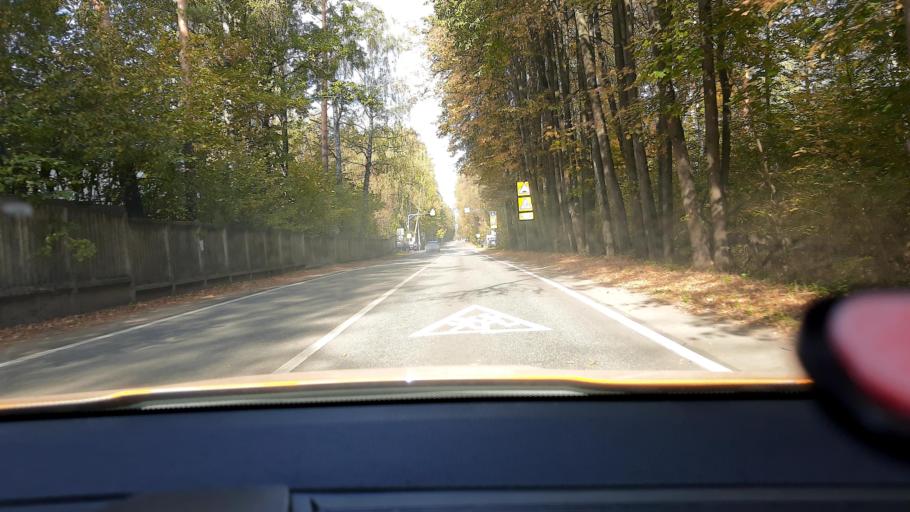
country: RU
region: Moskovskaya
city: Petrovo-Dal'neye
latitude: 55.7889
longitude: 37.2081
